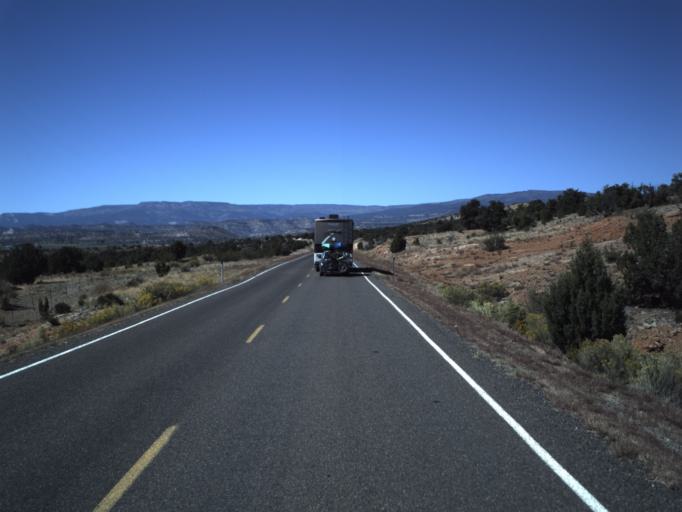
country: US
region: Utah
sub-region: Wayne County
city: Loa
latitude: 37.7332
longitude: -111.5401
